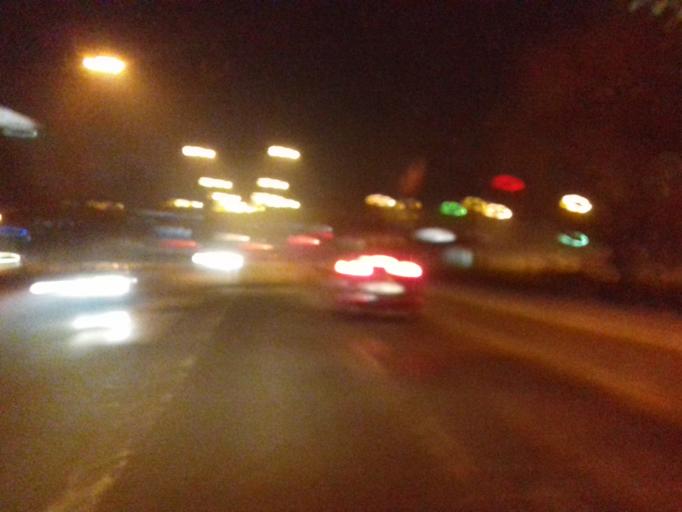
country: BA
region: Federation of Bosnia and Herzegovina
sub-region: Kanton Sarajevo
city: Sarajevo
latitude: 43.8442
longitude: 18.3480
